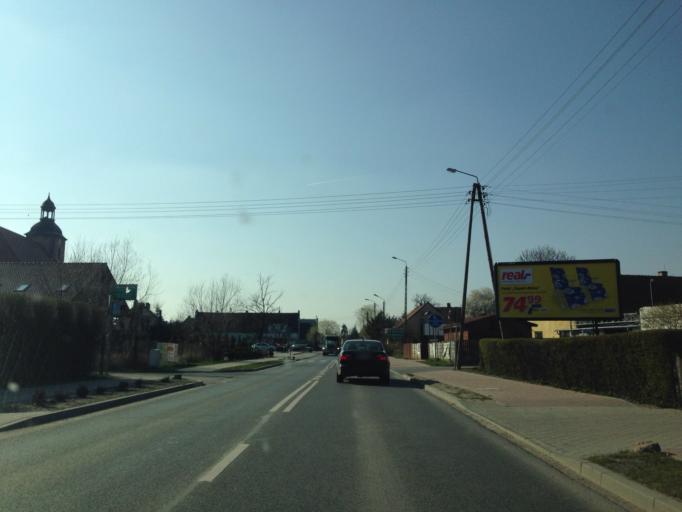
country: PL
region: Lower Silesian Voivodeship
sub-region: Powiat wroclawski
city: Kielczow
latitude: 51.1391
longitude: 17.1815
